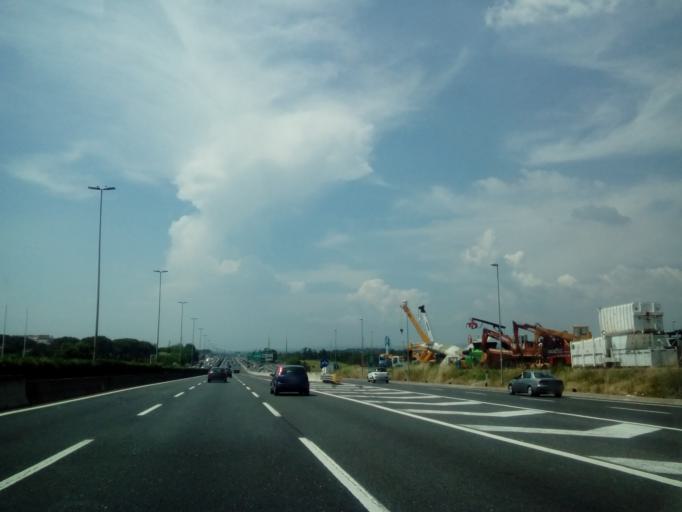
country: IT
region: Latium
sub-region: Citta metropolitana di Roma Capitale
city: Colle Verde
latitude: 41.9740
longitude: 12.5464
